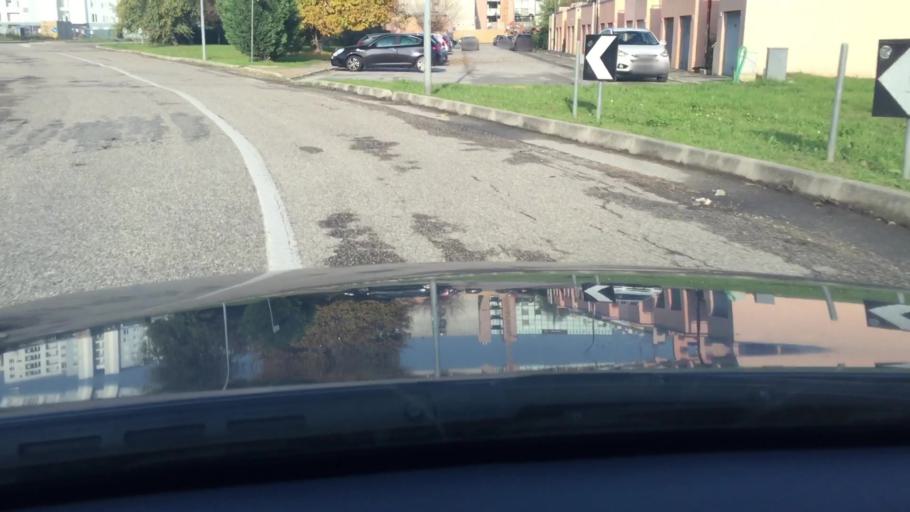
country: IT
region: Emilia-Romagna
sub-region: Provincia di Ferrara
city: Ferrara
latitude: 44.8182
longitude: 11.5964
